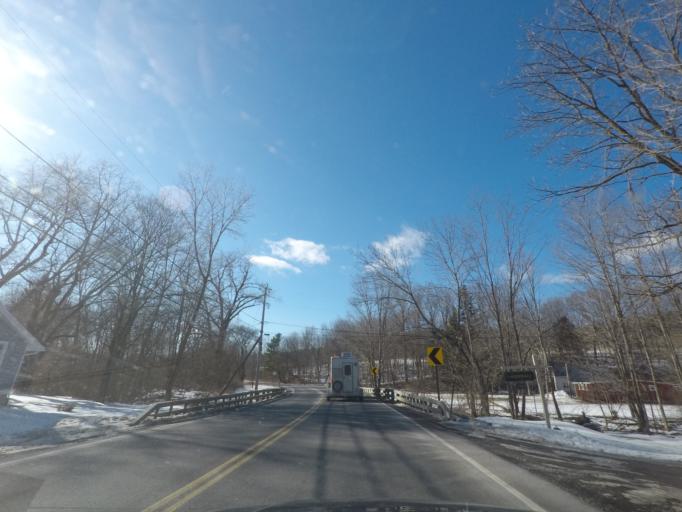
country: US
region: New York
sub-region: Columbia County
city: Chatham
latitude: 42.4208
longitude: -73.4968
